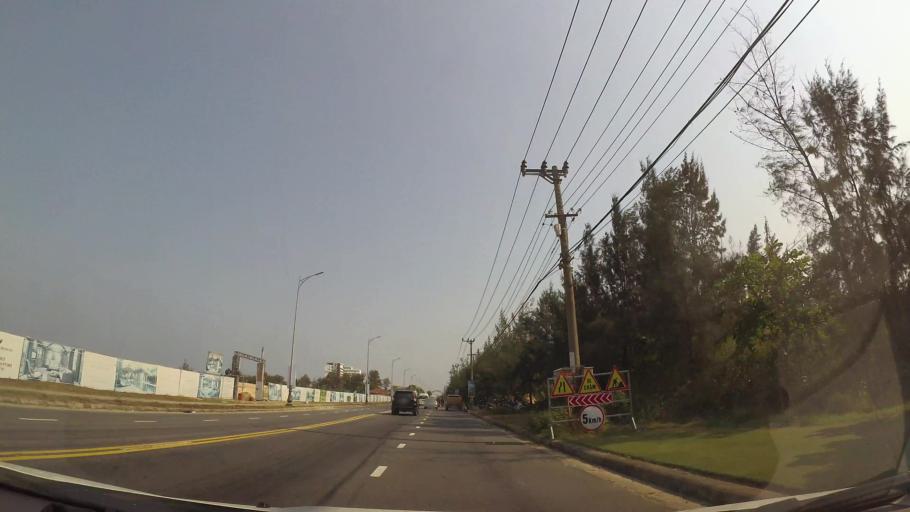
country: VN
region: Da Nang
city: Ngu Hanh Son
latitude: 15.9724
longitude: 108.2811
